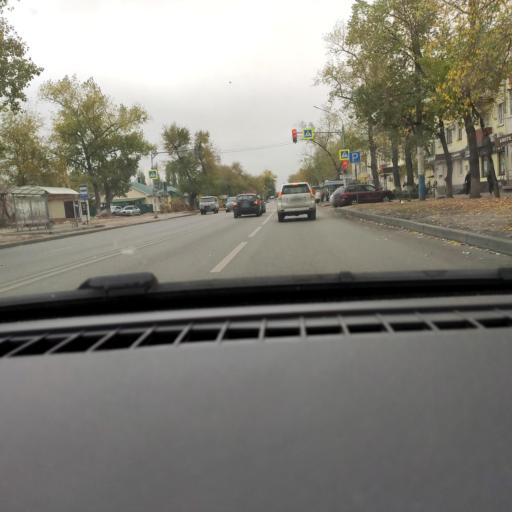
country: RU
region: Voronezj
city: Somovo
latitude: 51.7167
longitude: 39.2743
